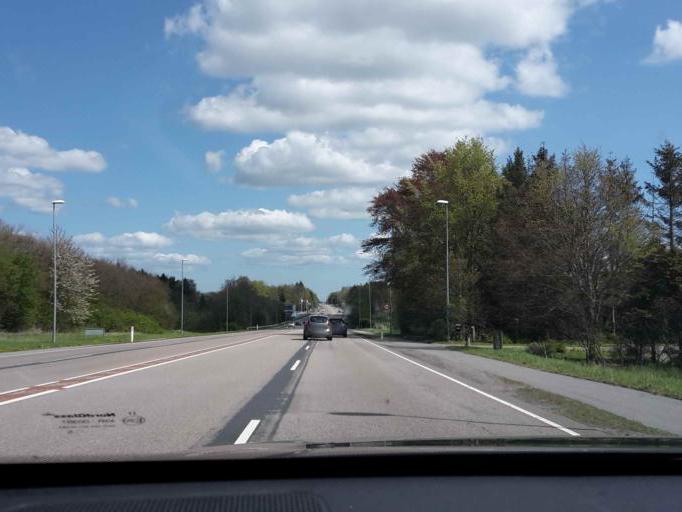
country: DK
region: South Denmark
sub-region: Assens Kommune
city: Tommerup Stationsby
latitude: 55.3891
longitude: 10.2356
